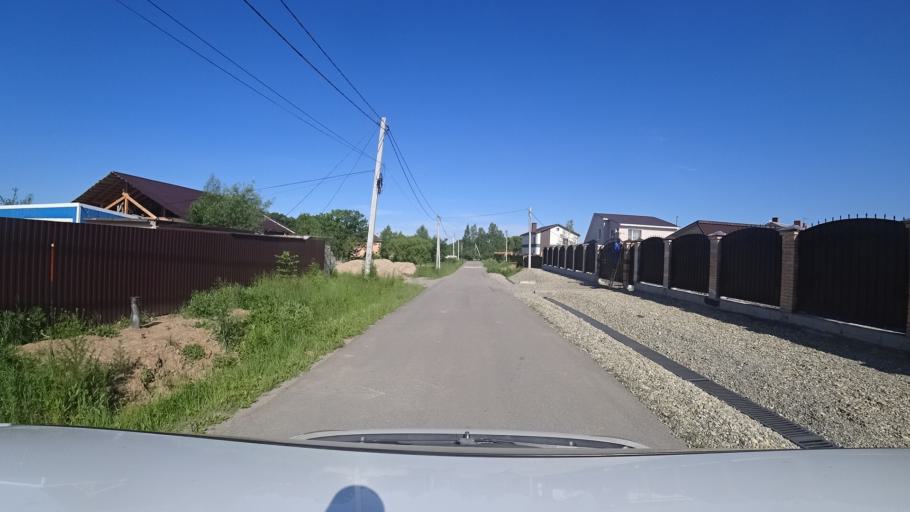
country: RU
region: Khabarovsk Krai
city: Topolevo
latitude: 48.5482
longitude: 135.1815
